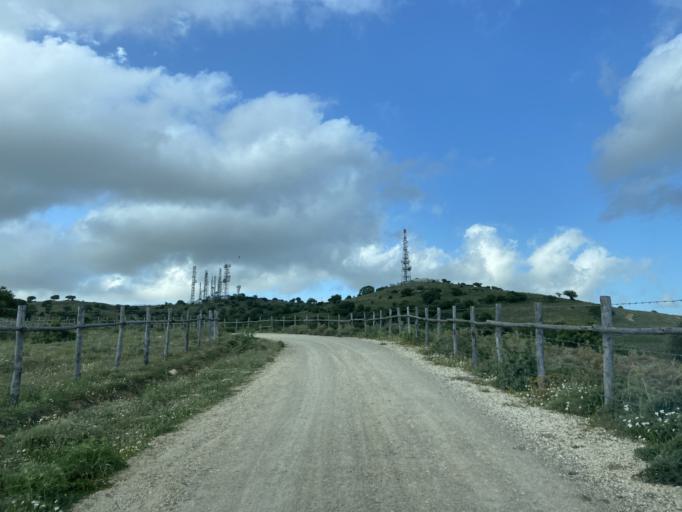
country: IT
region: Latium
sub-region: Citta metropolitana di Roma Capitale
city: Santa Marinella
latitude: 42.0849
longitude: 11.8527
